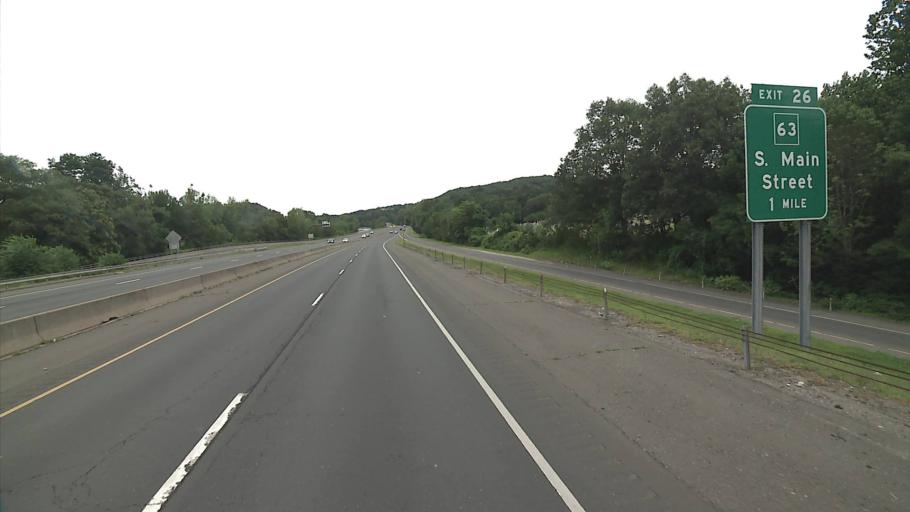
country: US
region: Connecticut
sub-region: New Haven County
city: Naugatuck
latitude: 41.4696
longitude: -73.0511
